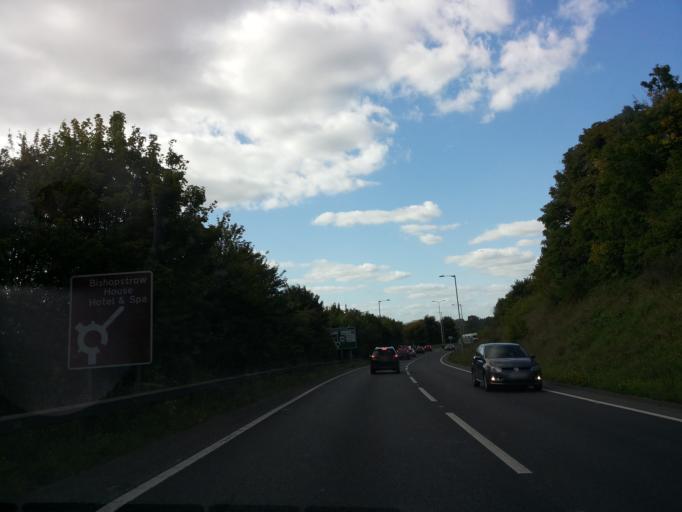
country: GB
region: England
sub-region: Wiltshire
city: Bishopstrow
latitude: 51.1849
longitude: -2.1170
